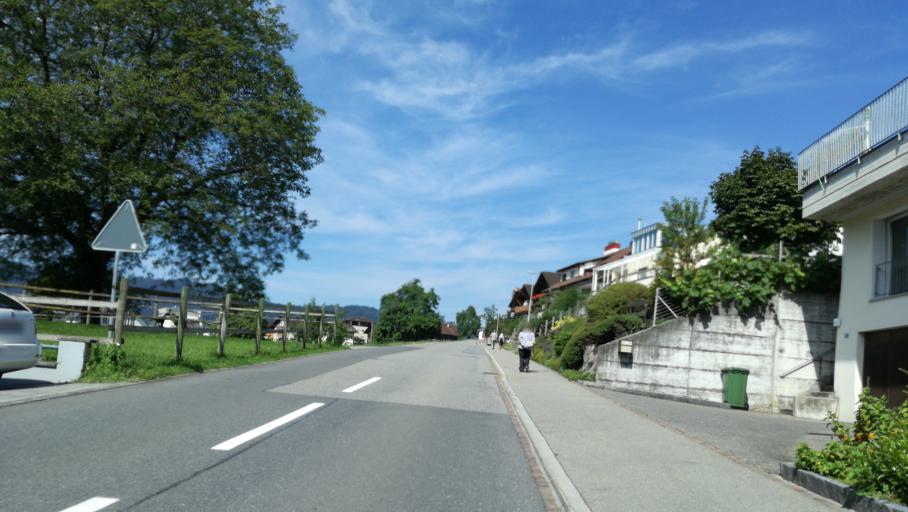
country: CH
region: Zug
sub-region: Zug
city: Unterageri
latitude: 47.1397
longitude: 8.5808
